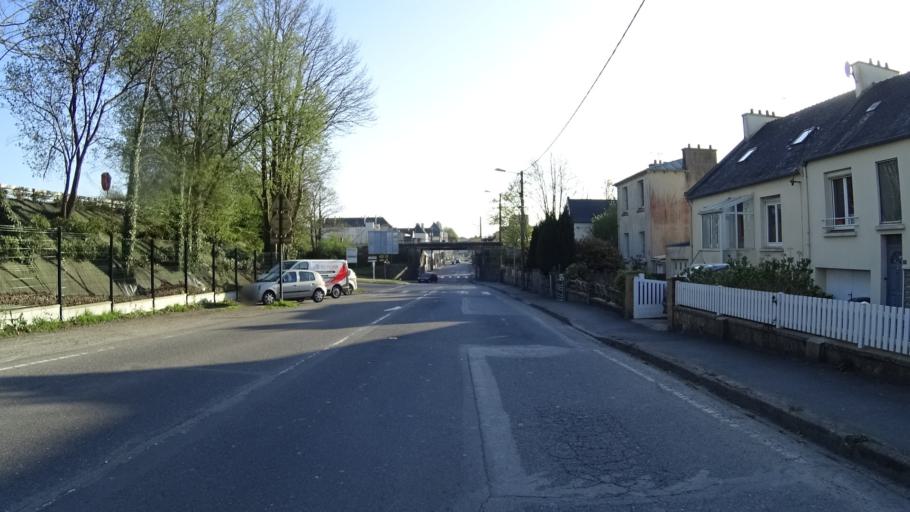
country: FR
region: Brittany
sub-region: Departement du Finistere
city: Landerneau
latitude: 48.4541
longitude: -4.2394
